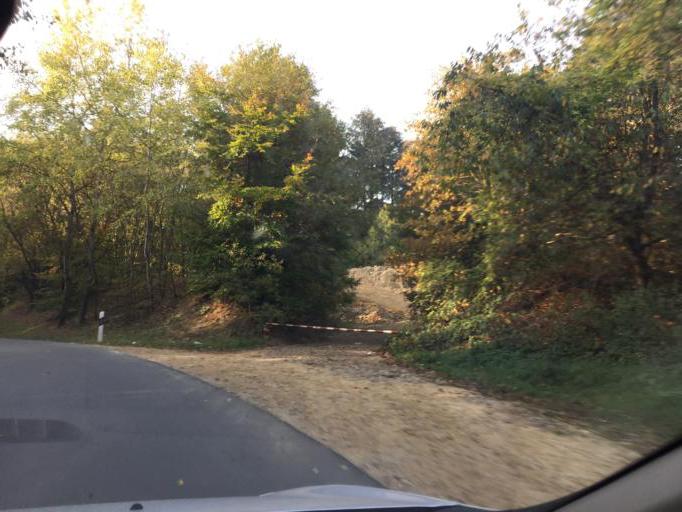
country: LU
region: Luxembourg
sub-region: Canton de Luxembourg
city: Contern
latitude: 49.5715
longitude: 6.2165
